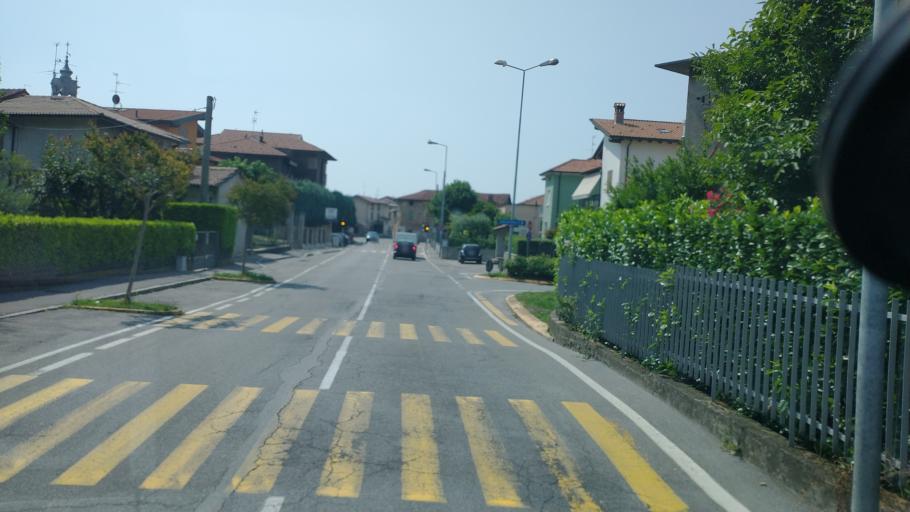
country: IT
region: Lombardy
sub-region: Provincia di Bergamo
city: Levate
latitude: 45.6263
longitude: 9.6217
